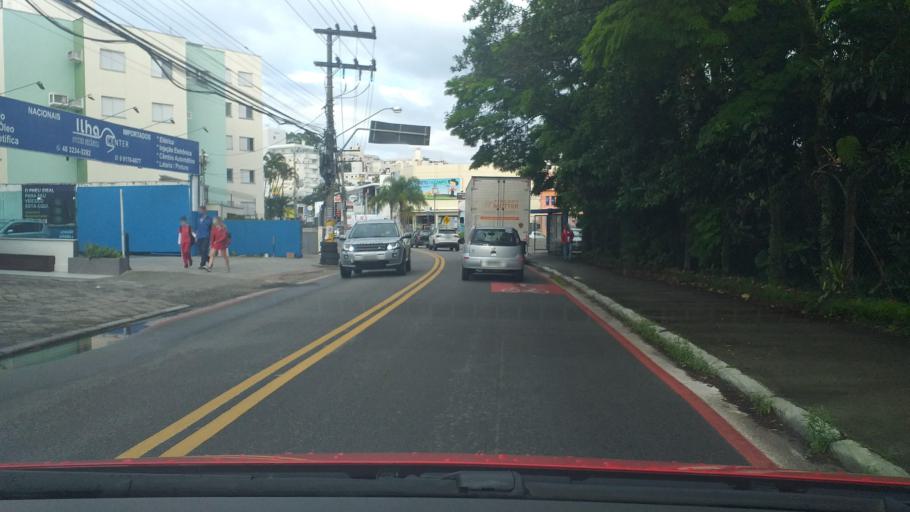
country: BR
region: Santa Catarina
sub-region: Florianopolis
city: Corrego Grande
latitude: -27.5999
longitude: -48.5119
